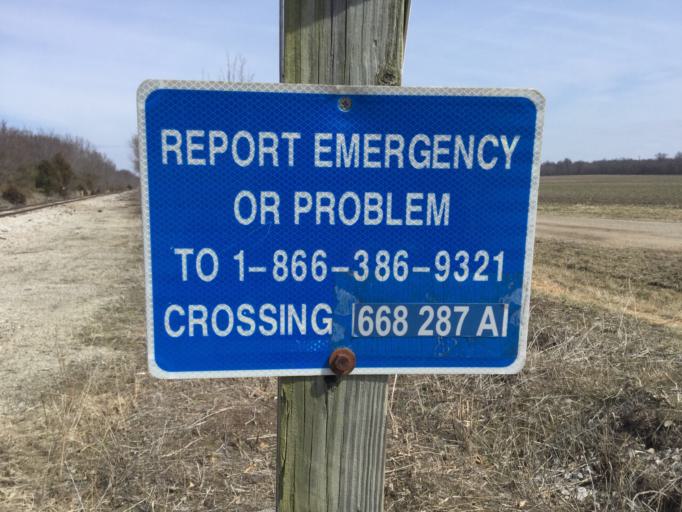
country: US
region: Kansas
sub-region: Labette County
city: Oswego
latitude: 37.1747
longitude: -94.9953
